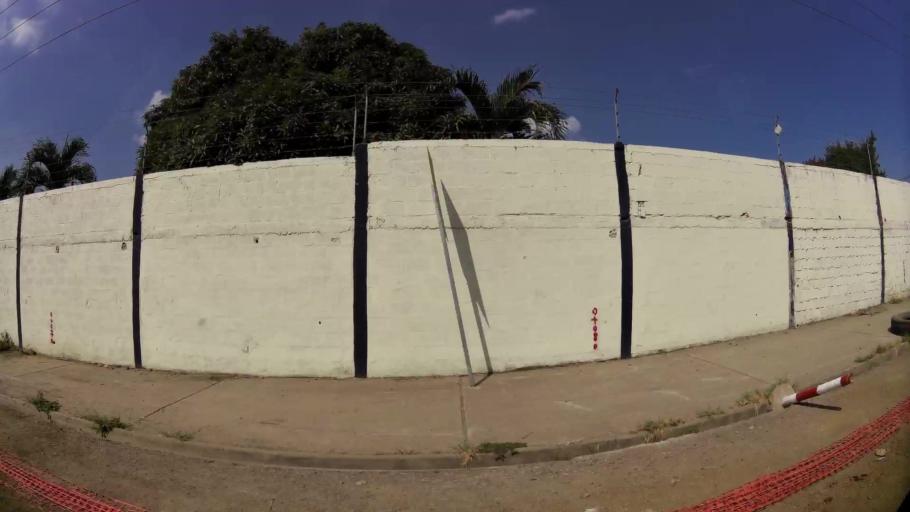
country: EC
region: Guayas
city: Guayaquil
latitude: -2.1444
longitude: -79.9406
